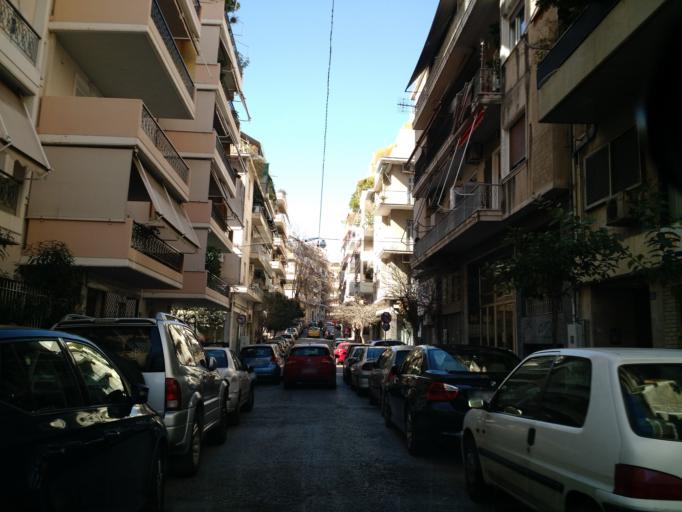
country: GR
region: Attica
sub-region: Nomarchia Athinas
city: Psychiko
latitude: 37.9898
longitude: 23.7631
